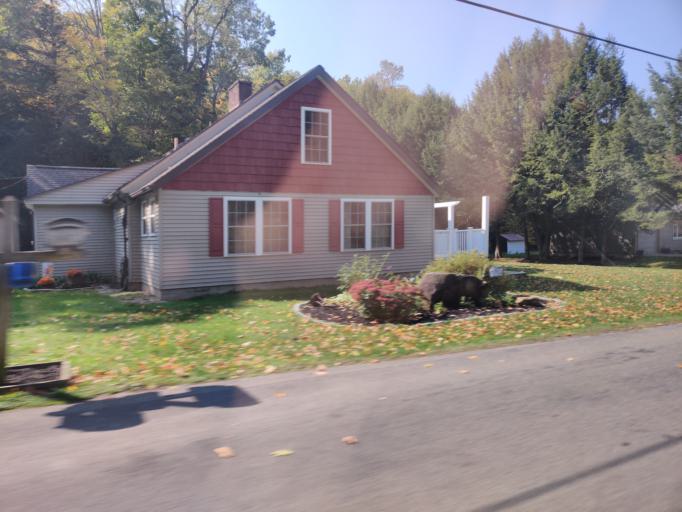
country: US
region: Pennsylvania
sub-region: Warren County
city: Warren
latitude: 41.8186
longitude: -79.0953
